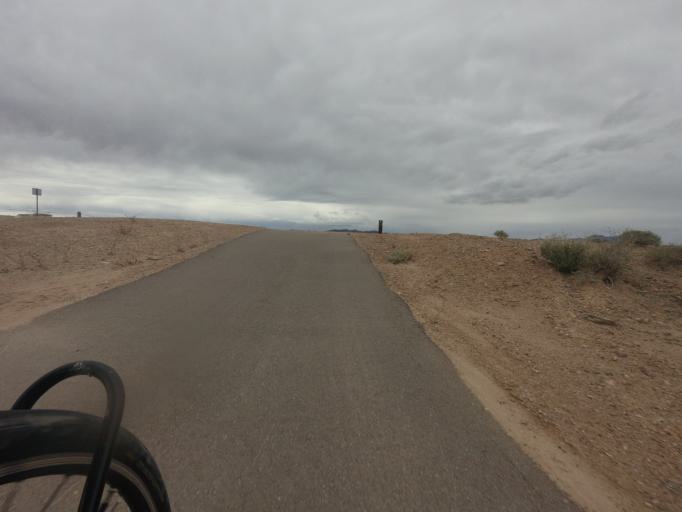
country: US
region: Nevada
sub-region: Clark County
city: Henderson
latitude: 36.1031
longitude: -114.9988
